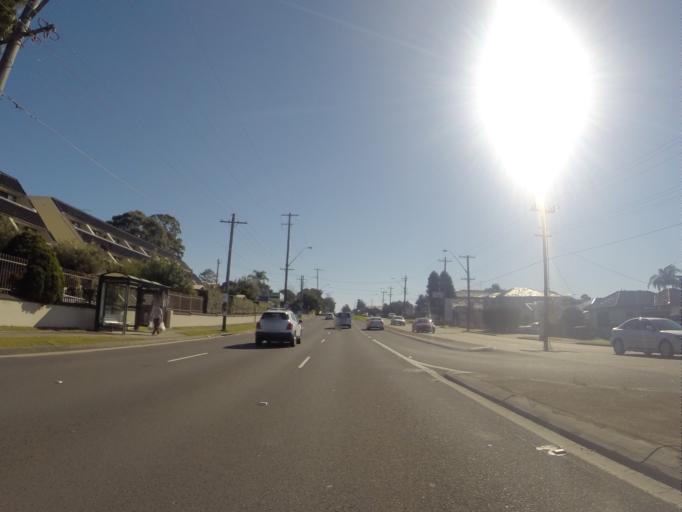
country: AU
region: New South Wales
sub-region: Kogarah
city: Kogarah
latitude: -33.9807
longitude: 151.1076
